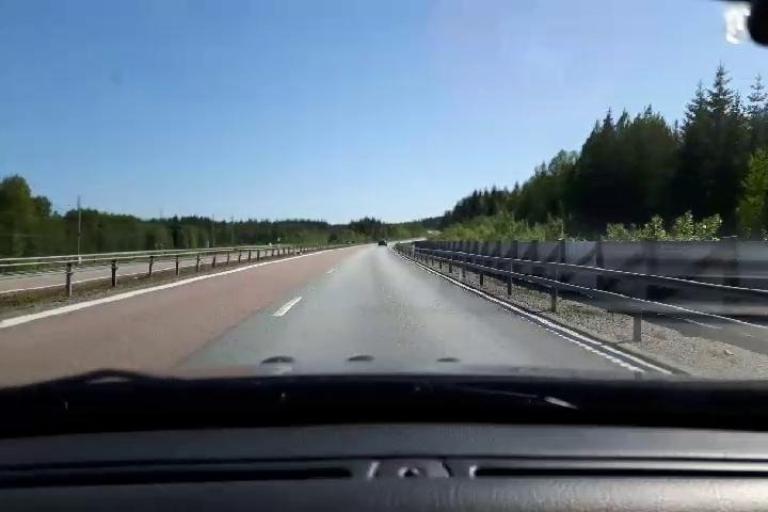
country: SE
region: Gaevleborg
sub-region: Soderhamns Kommun
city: Soderhamn
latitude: 61.4061
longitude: 16.9940
